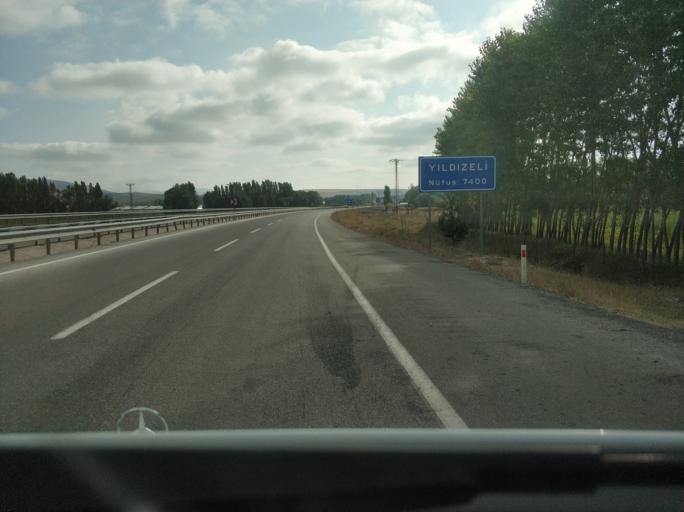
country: TR
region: Sivas
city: Yildizeli
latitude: 39.8679
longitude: 36.5818
